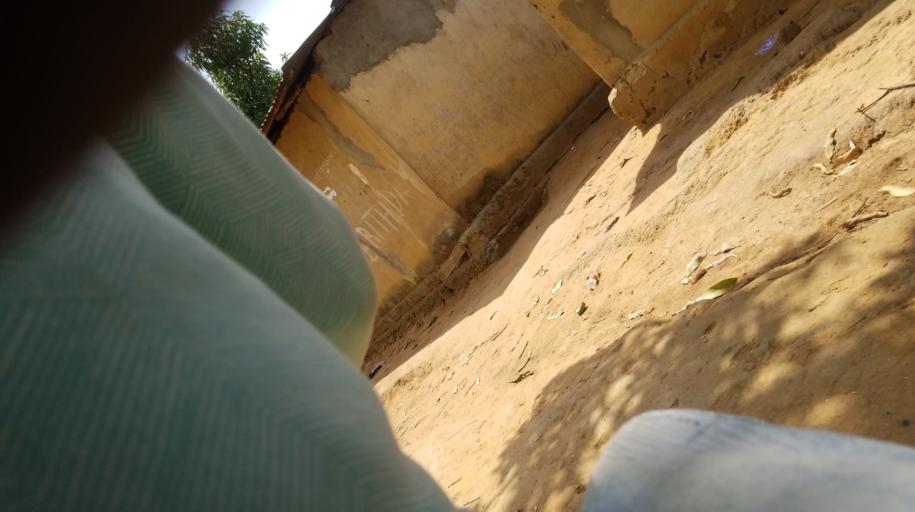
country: SL
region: Western Area
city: Waterloo
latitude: 8.3233
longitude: -13.0556
